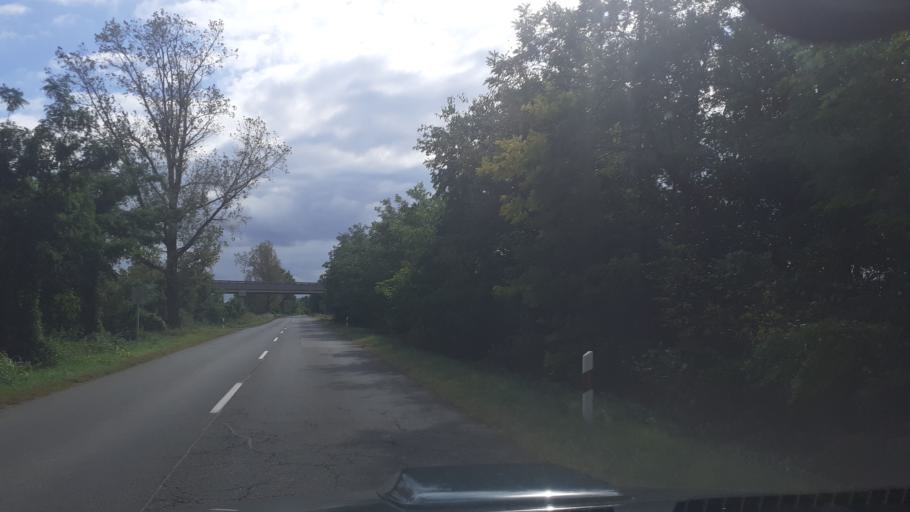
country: HU
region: Bacs-Kiskun
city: Apostag
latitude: 46.8757
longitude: 18.9786
